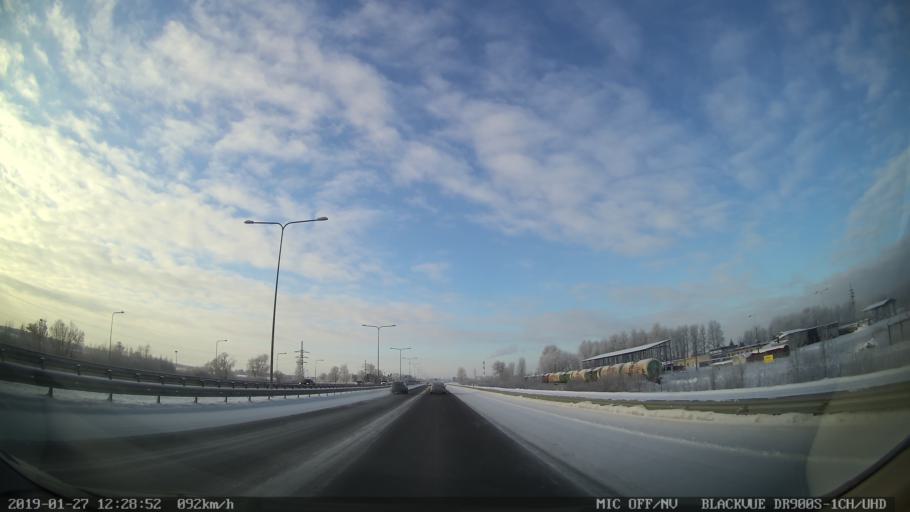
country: EE
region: Harju
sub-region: Maardu linn
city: Maardu
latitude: 59.4524
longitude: 25.0040
